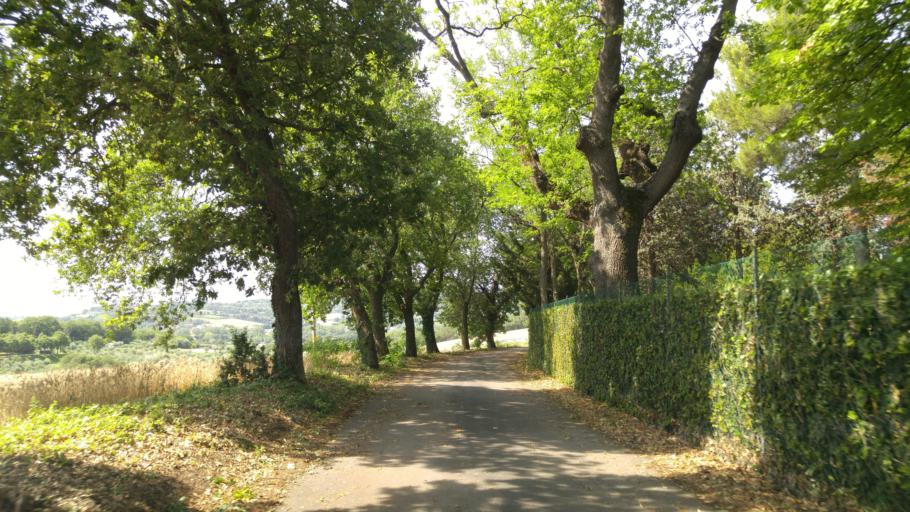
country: IT
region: The Marches
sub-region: Provincia di Pesaro e Urbino
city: Centinarola
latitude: 43.8495
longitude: 12.9877
